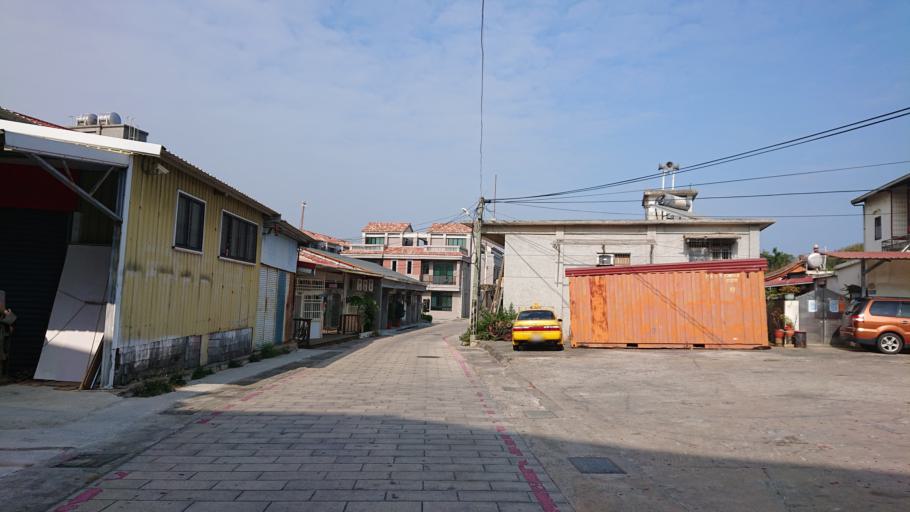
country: TW
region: Fukien
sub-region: Kinmen
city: Jincheng
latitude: 24.4799
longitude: 118.4280
